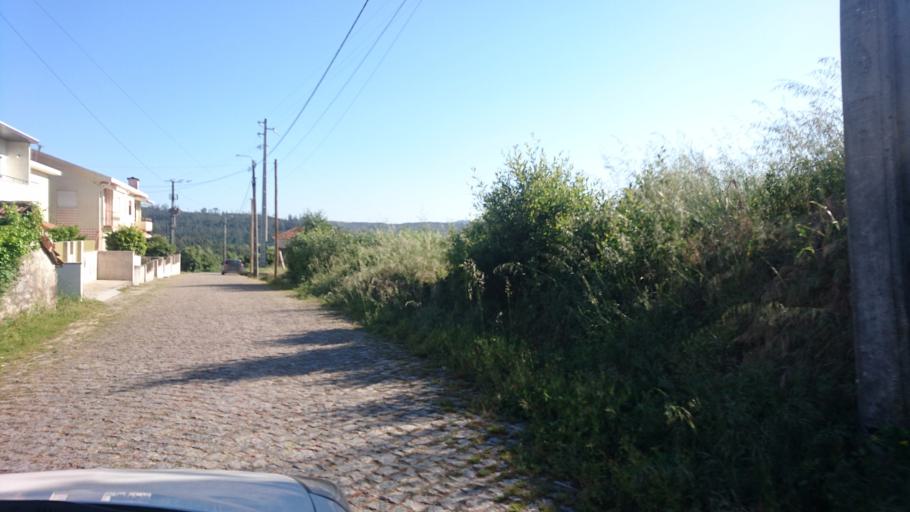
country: PT
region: Porto
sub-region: Paredes
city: Baltar
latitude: 41.1608
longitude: -8.3787
